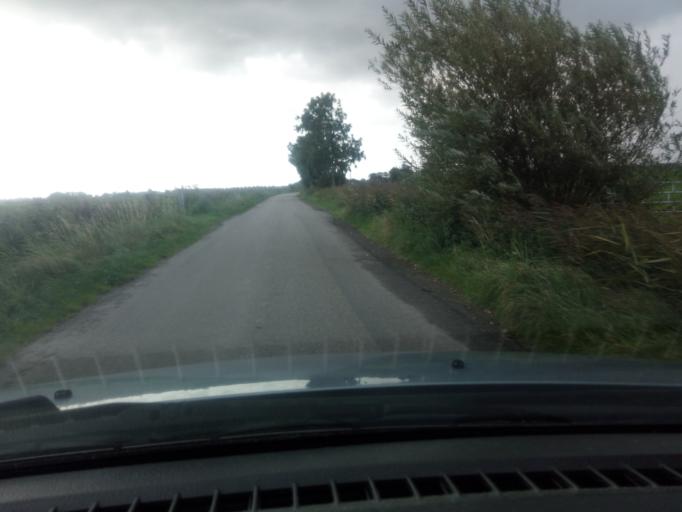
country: NL
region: Groningen
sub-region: Gemeente Grootegast
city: Grootegast
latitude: 53.2604
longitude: 6.2469
